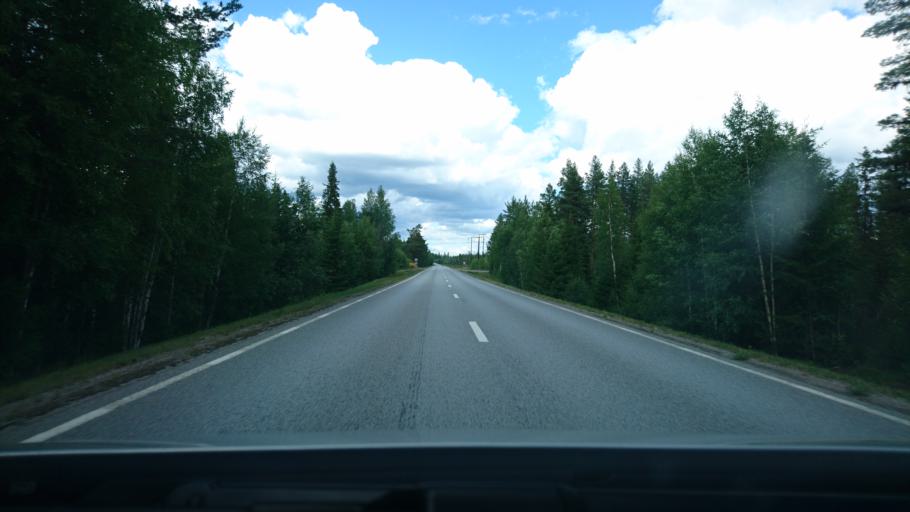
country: SE
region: Vaesterbotten
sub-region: Asele Kommun
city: Asele
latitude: 63.7381
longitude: 16.9952
